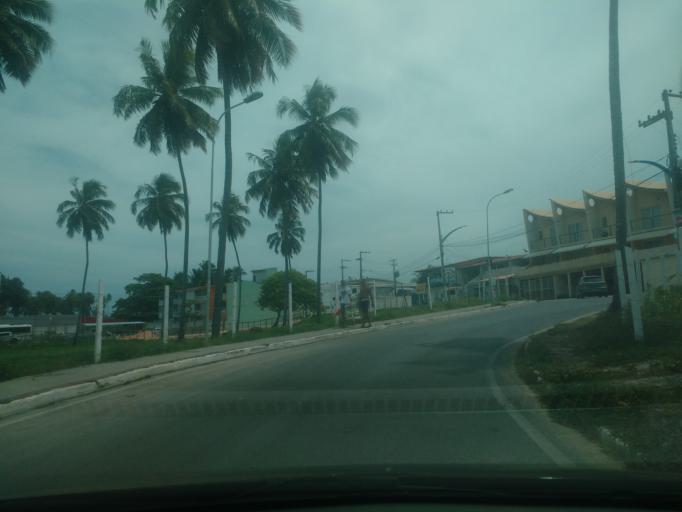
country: BR
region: Alagoas
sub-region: Marechal Deodoro
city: Marechal Deodoro
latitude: -9.7687
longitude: -35.8435
